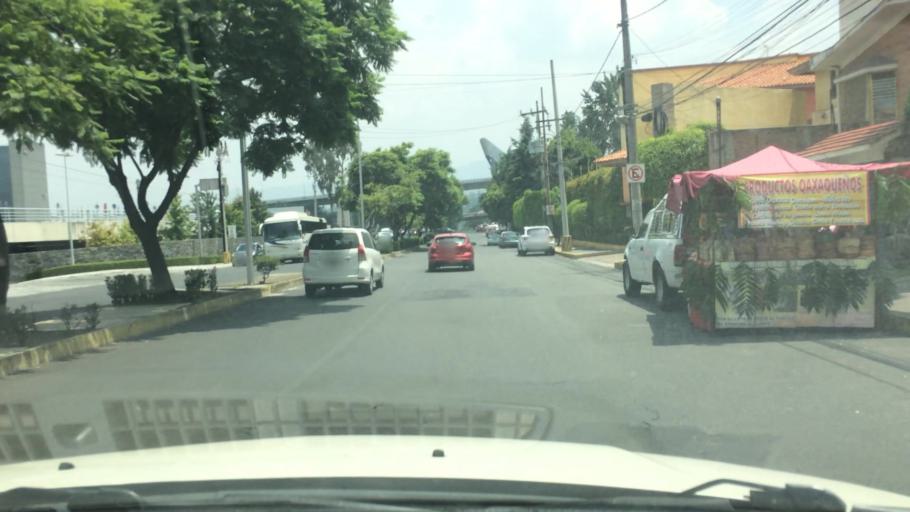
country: MX
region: Mexico City
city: Tlalpan
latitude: 19.3053
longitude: -99.1934
